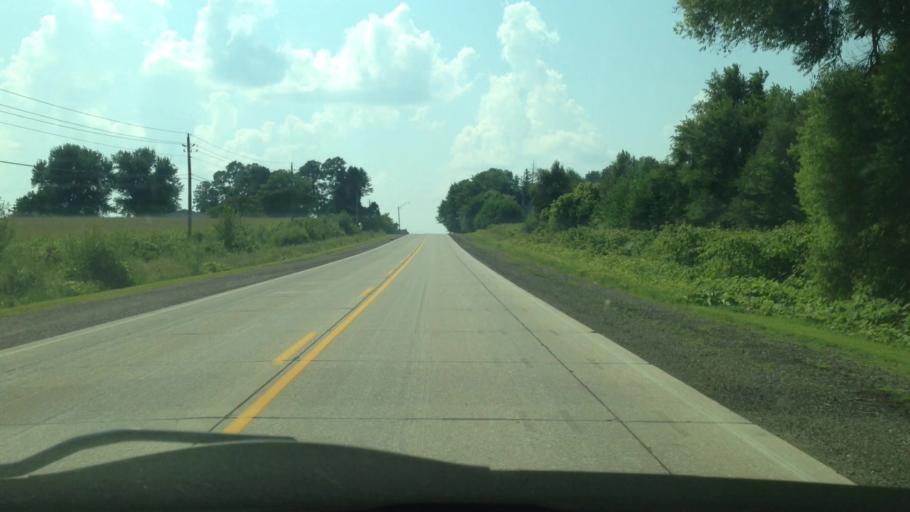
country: US
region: Iowa
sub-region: Black Hawk County
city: Waterloo
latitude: 42.5422
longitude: -92.3426
